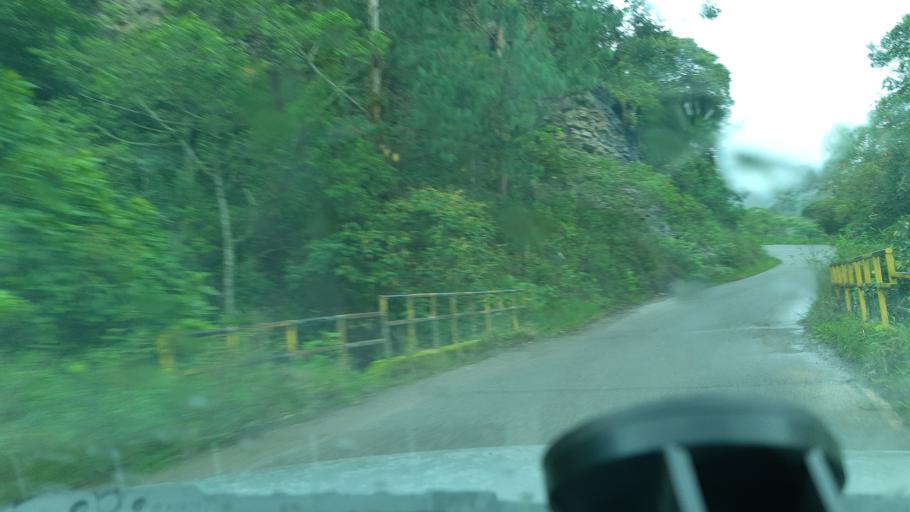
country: CO
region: Boyaca
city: Chinavita
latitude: 5.1932
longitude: -73.3822
